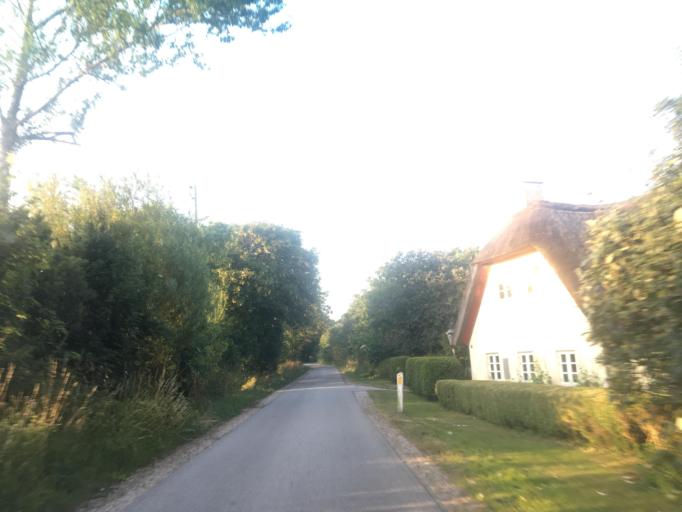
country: DK
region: North Denmark
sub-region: Thisted Kommune
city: Hurup
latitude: 56.8406
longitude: 8.3566
